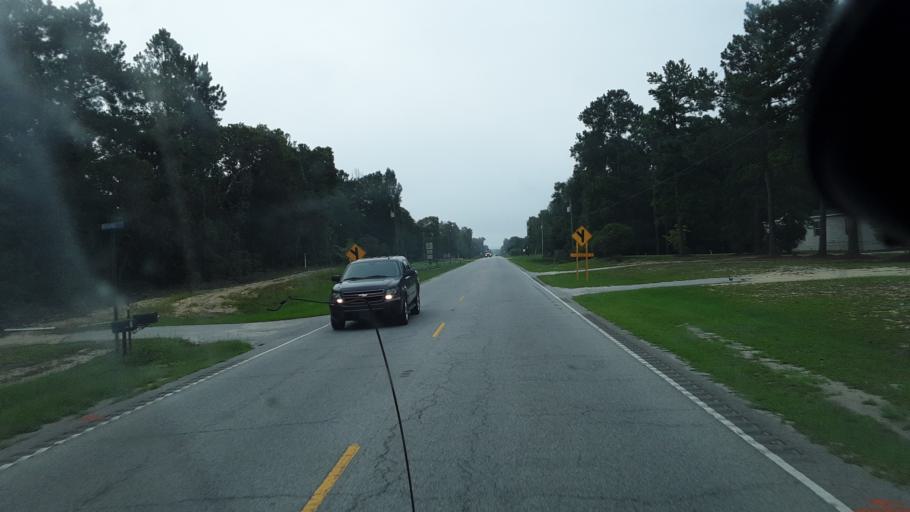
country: US
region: South Carolina
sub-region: Florence County
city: Johnsonville
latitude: 33.8934
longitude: -79.3858
